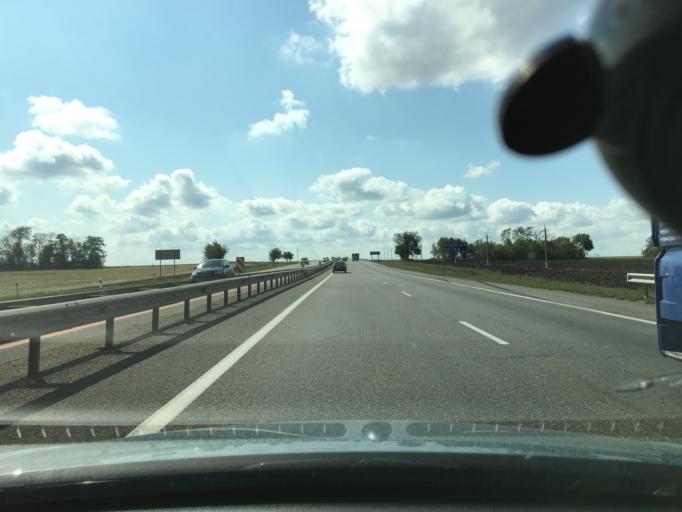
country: RU
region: Krasnodarskiy
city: Krasnoye
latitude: 46.7280
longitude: 39.6555
